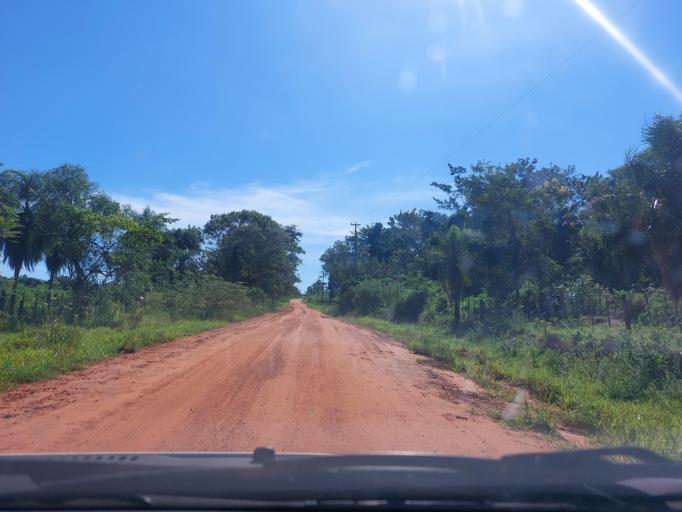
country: PY
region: San Pedro
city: Itacurubi del Rosario
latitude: -24.5447
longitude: -56.5847
